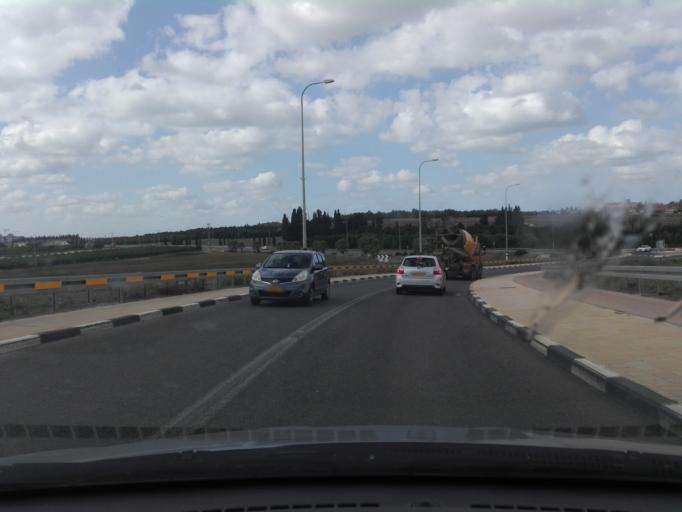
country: IL
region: Haifa
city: Qesarya
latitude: 32.5100
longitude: 34.9490
